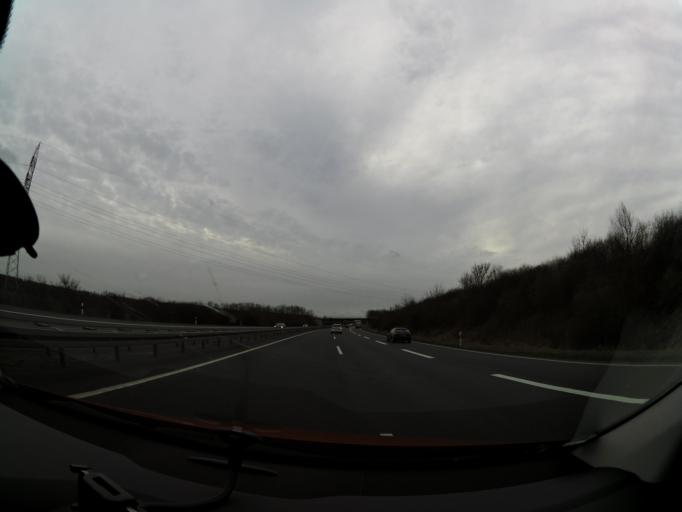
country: DE
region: Lower Saxony
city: Leiferde
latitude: 52.2057
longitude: 10.5332
